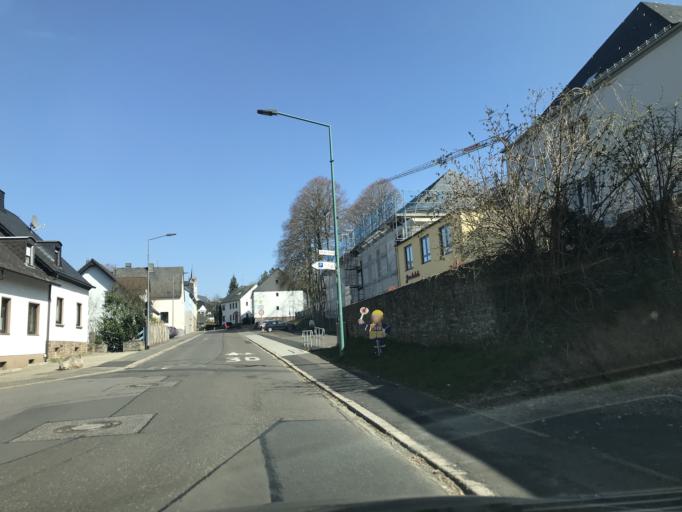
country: DE
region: Rheinland-Pfalz
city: Hermeskeil
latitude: 49.6534
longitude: 6.9423
